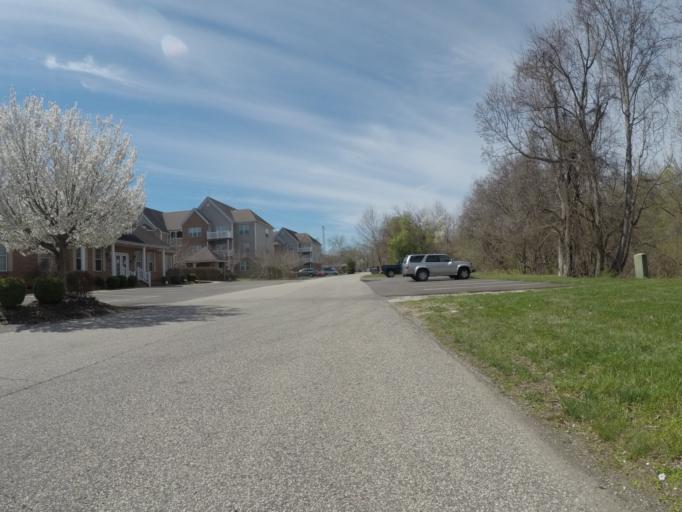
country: US
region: West Virginia
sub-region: Cabell County
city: Pea Ridge
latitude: 38.4109
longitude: -82.3141
